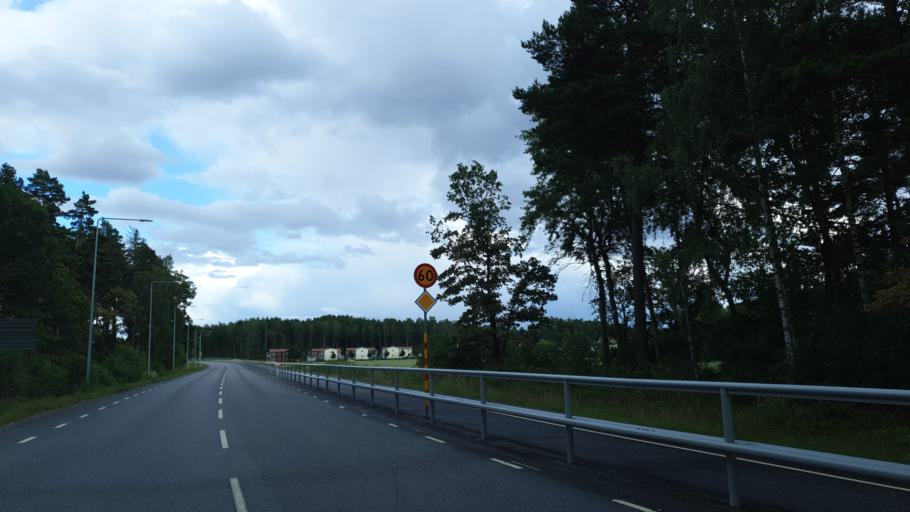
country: SE
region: Stockholm
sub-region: Jarfalla Kommun
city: Jakobsberg
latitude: 59.4260
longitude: 17.7997
